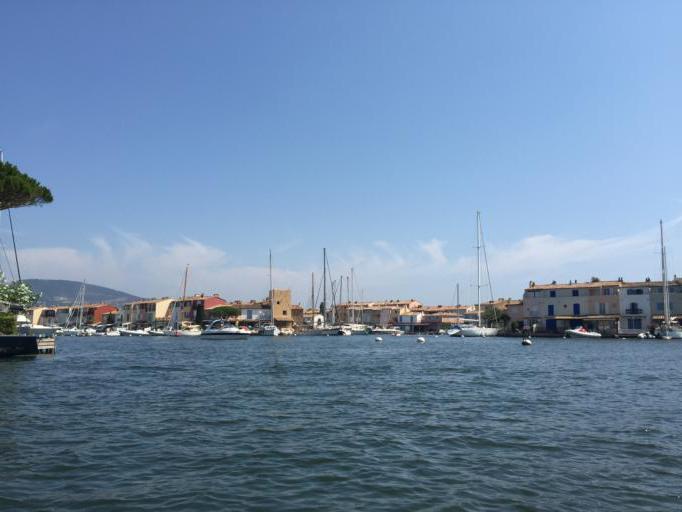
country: FR
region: Provence-Alpes-Cote d'Azur
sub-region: Departement du Var
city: Gassin
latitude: 43.2720
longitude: 6.5815
